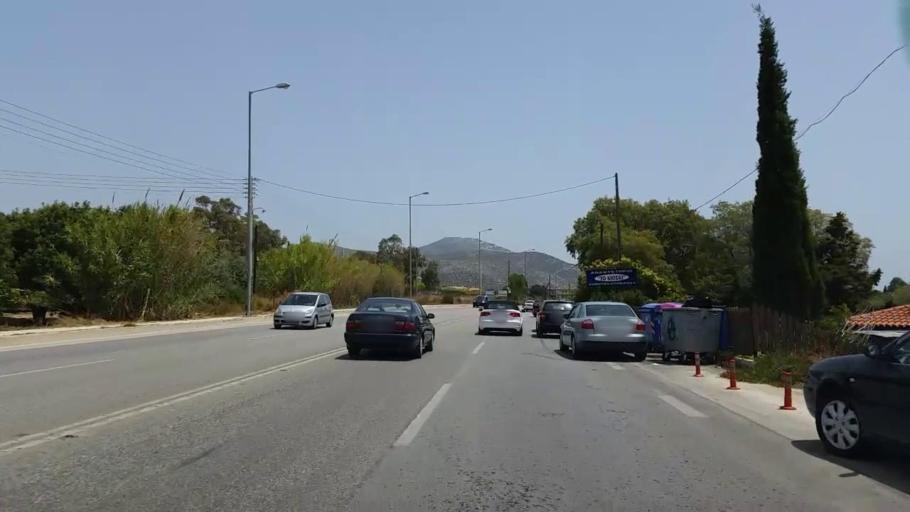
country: GR
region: Attica
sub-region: Nomarchia Anatolikis Attikis
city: Agios Dimitrios Kropias
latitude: 37.7850
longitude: 23.8876
